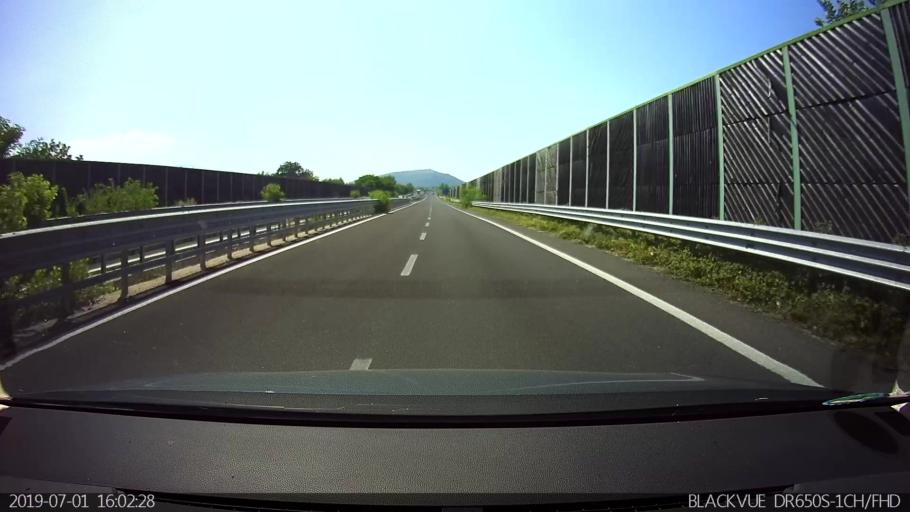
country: IT
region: Latium
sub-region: Provincia di Frosinone
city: Tecchiena
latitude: 41.6703
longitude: 13.3561
